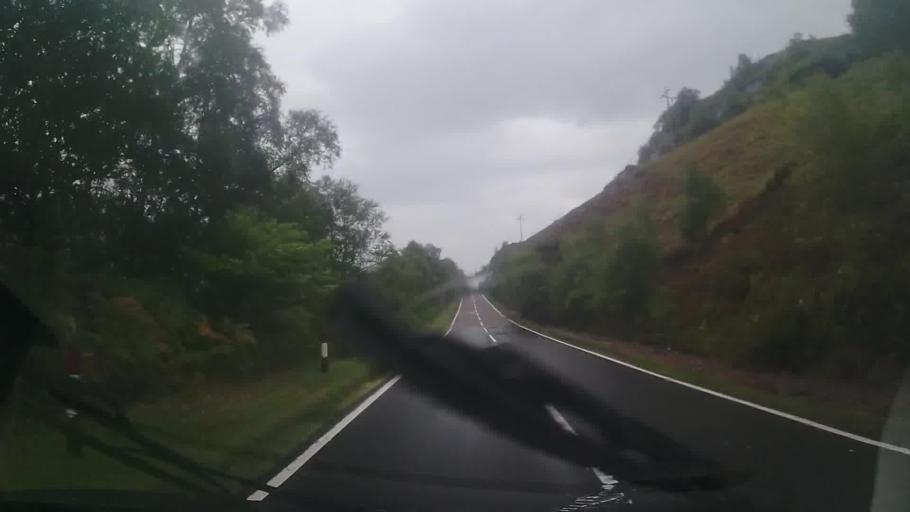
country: GB
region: Scotland
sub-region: Argyll and Bute
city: Isle Of Mull
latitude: 56.8836
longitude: -5.6029
